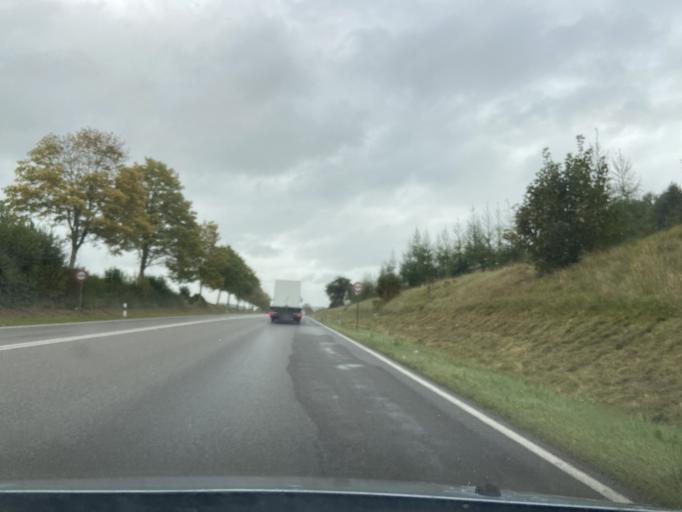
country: DE
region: Baden-Wuerttemberg
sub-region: Tuebingen Region
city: Messkirch
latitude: 47.9996
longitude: 9.1409
